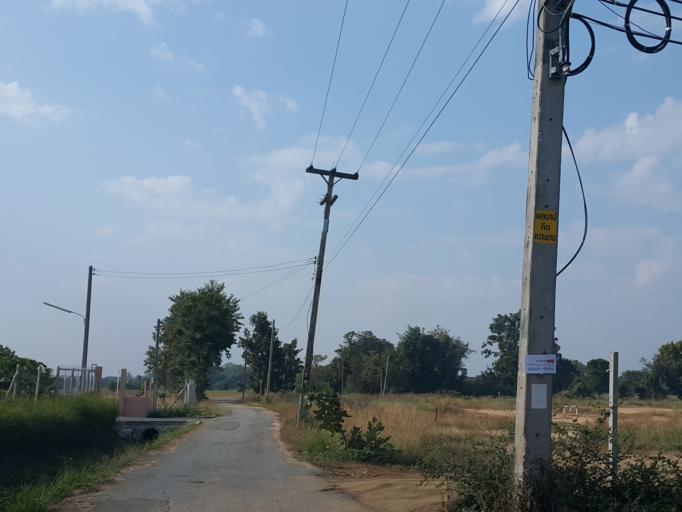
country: TH
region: Chiang Mai
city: San Kamphaeng
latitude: 18.8249
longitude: 99.1223
